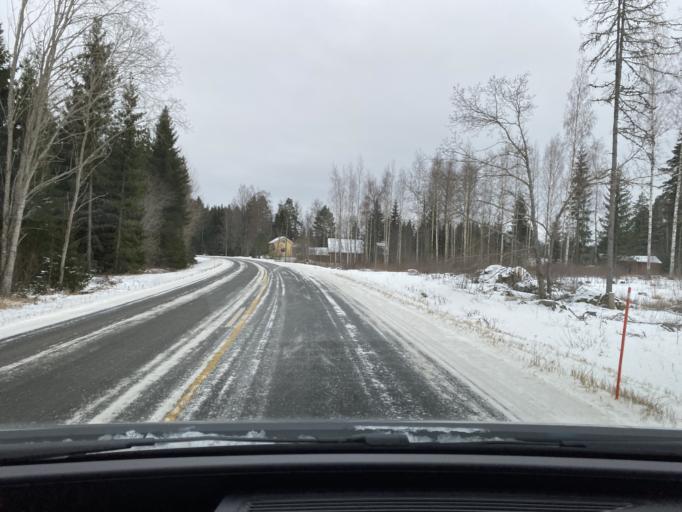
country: FI
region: Pirkanmaa
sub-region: Lounais-Pirkanmaa
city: Punkalaidun
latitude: 61.1900
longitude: 23.0381
